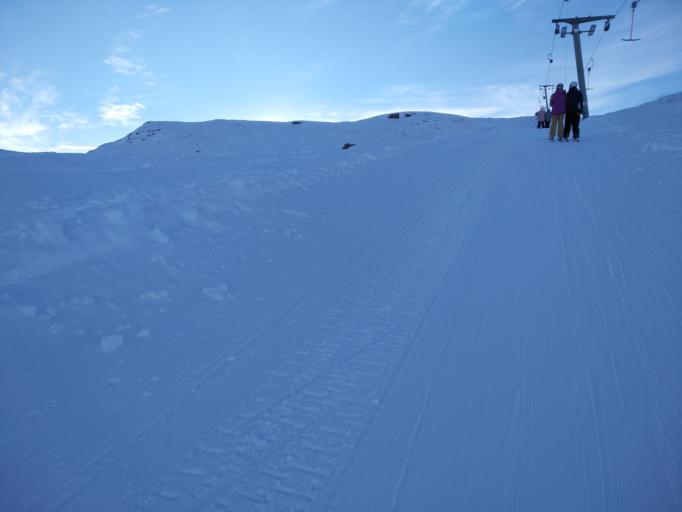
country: NO
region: Rogaland
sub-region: Sauda
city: Sauda
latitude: 59.6158
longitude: 6.2282
